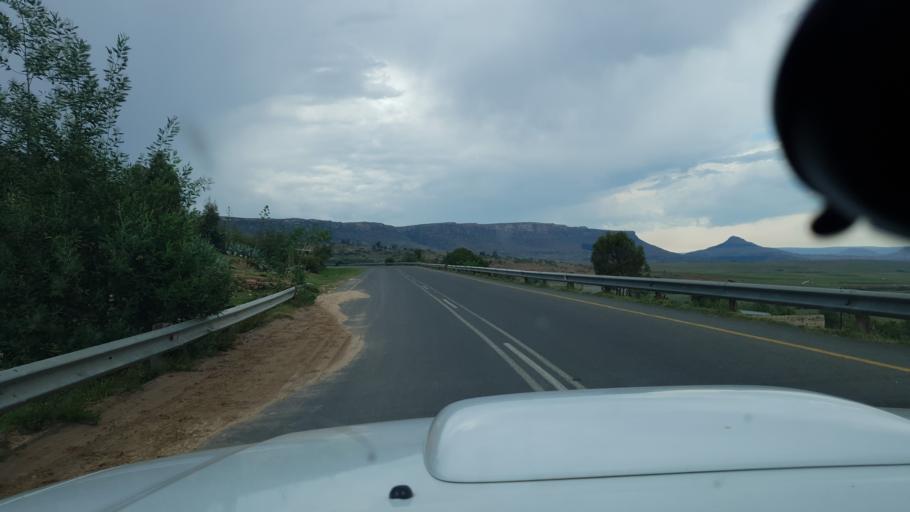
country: LS
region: Maseru
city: Maseru
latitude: -29.4670
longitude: 27.5055
